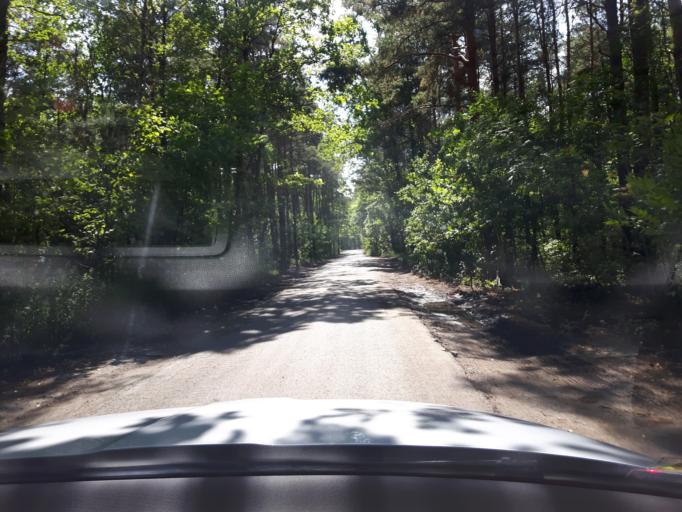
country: PL
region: Masovian Voivodeship
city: Zielonka
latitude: 52.2896
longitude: 21.1466
